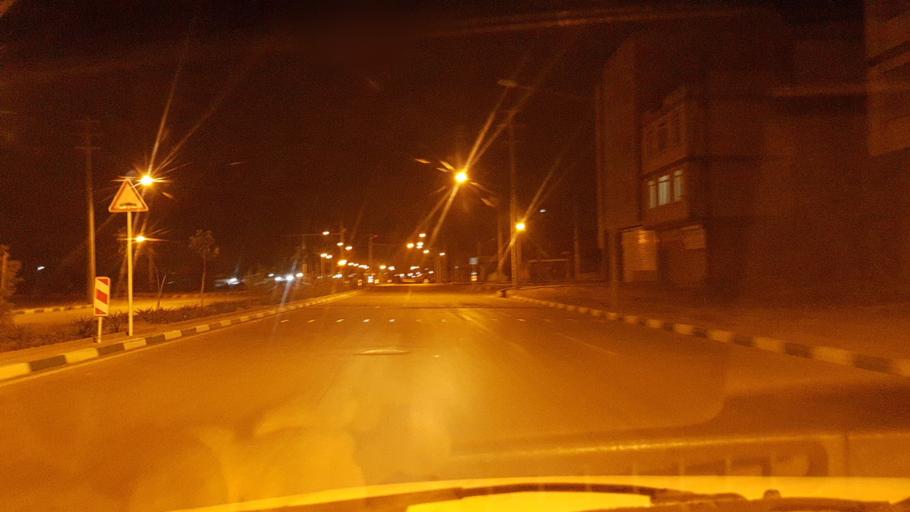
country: IR
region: Razavi Khorasan
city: Mashhad
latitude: 36.3565
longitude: 59.5656
